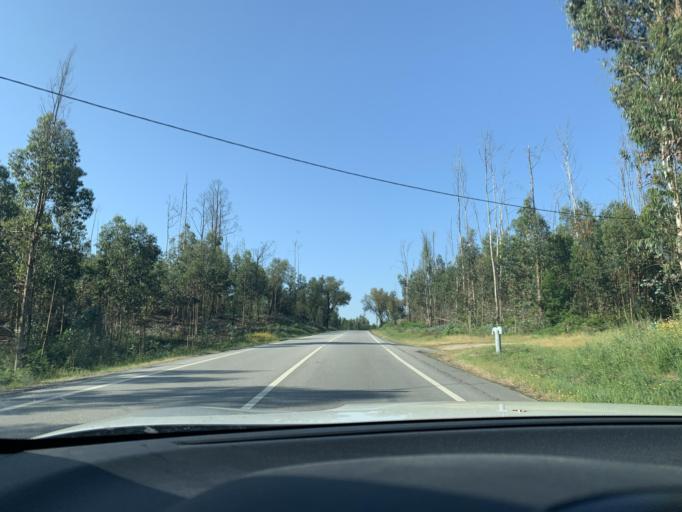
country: PT
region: Viseu
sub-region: Concelho de Tondela
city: Tondela
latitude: 40.4726
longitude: -8.0936
